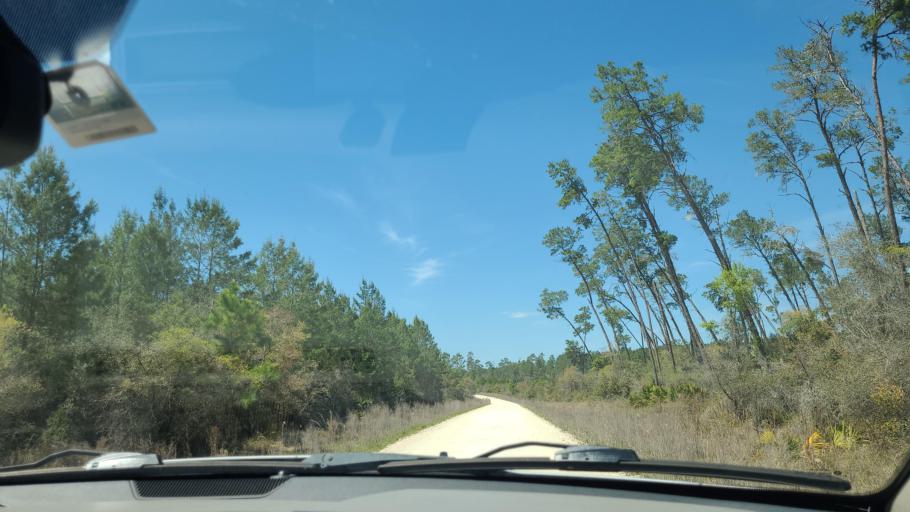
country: US
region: Florida
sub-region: Putnam County
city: Interlachen
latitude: 29.4369
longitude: -81.7616
